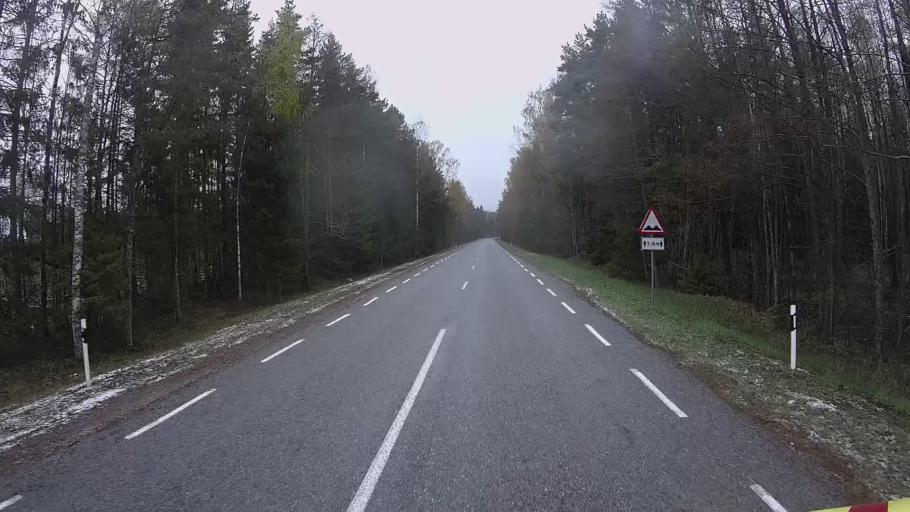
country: EE
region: Hiiumaa
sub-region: Kaerdla linn
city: Kardla
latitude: 59.0397
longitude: 22.6824
